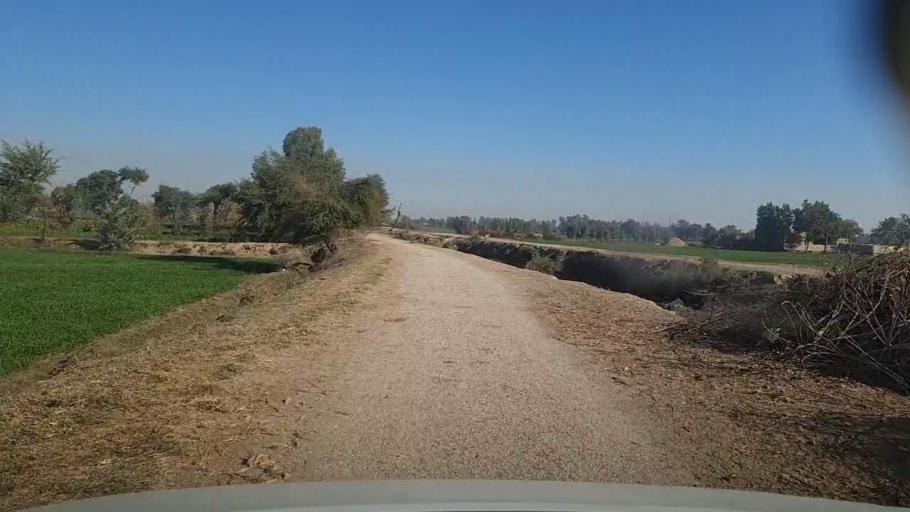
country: PK
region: Sindh
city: Khairpur
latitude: 28.0201
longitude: 69.6875
